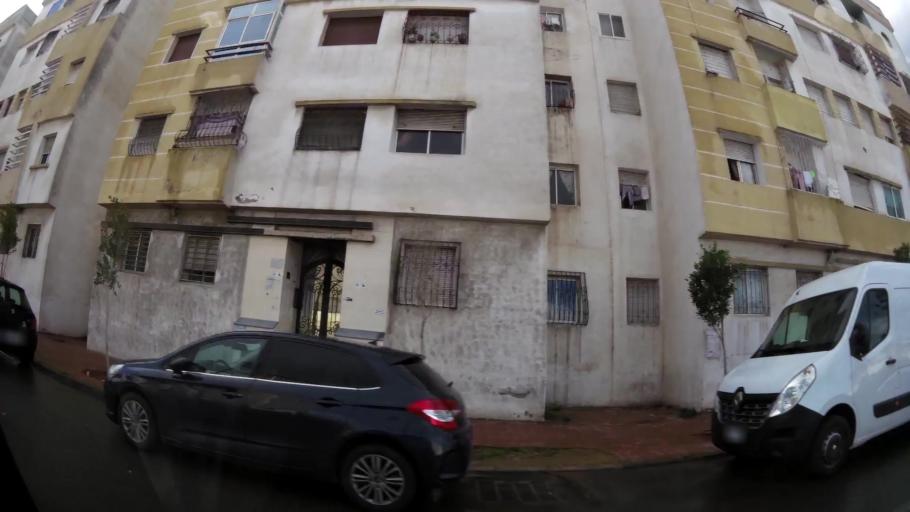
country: MA
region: Grand Casablanca
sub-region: Mediouna
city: Tit Mellil
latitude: 33.6011
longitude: -7.5331
